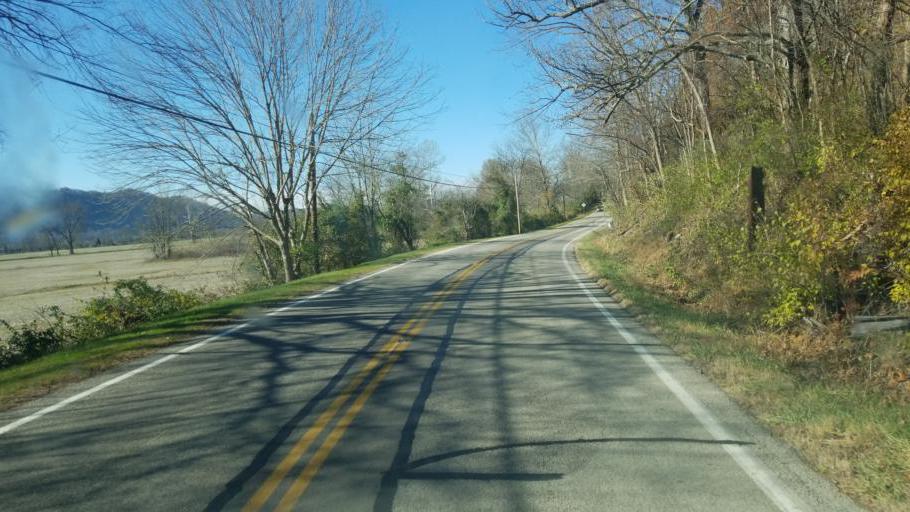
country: US
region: Kentucky
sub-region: Lewis County
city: Vanceburg
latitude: 38.6230
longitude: -83.1923
